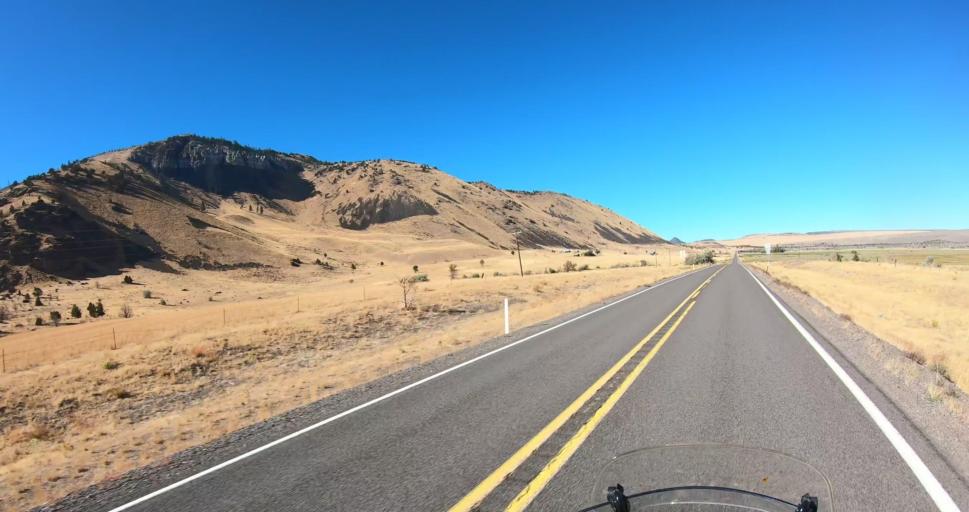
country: US
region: Oregon
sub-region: Lake County
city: Lakeview
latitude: 42.9770
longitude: -120.7777
